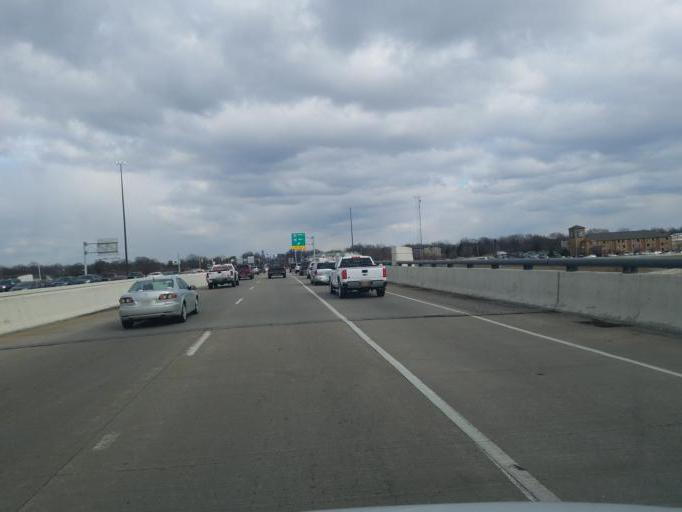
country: US
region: Indiana
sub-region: Marion County
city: Speedway
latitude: 39.7647
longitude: -86.2674
